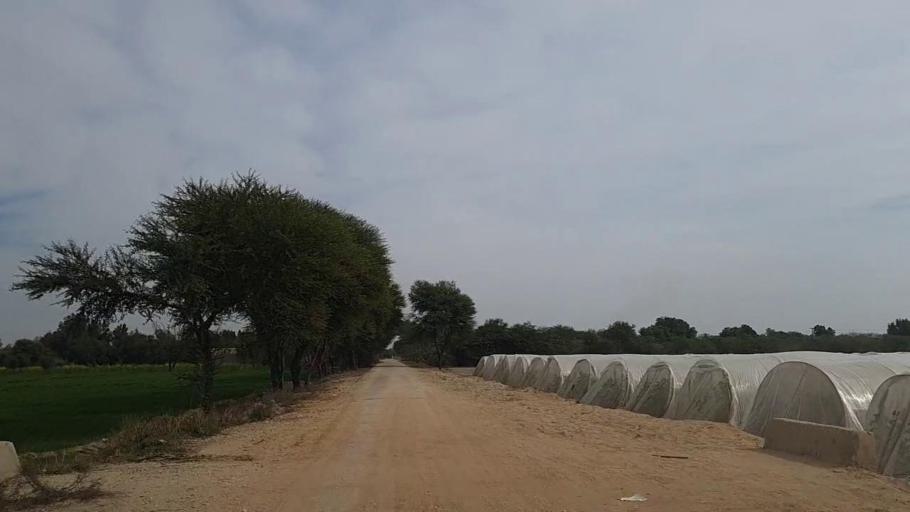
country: PK
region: Sindh
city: Daur
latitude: 26.4105
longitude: 68.4484
